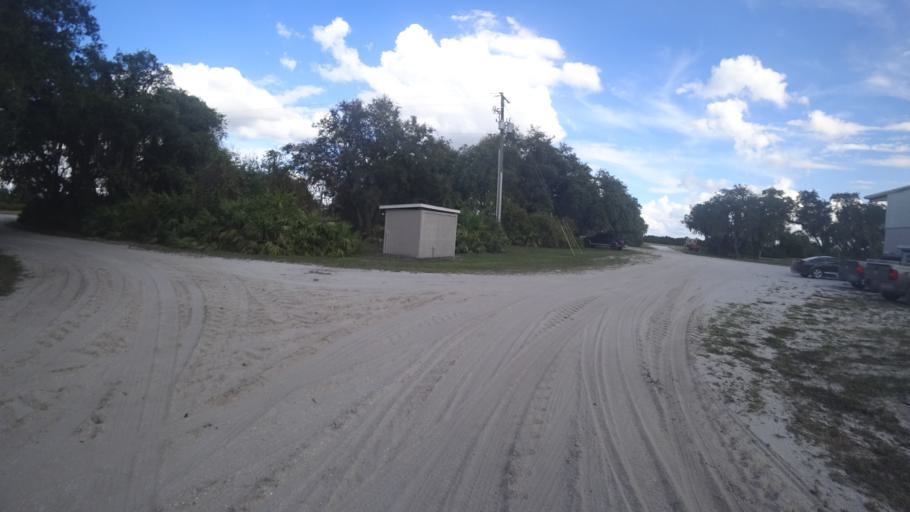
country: US
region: Florida
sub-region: Sarasota County
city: Warm Mineral Springs
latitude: 27.2997
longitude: -82.1244
